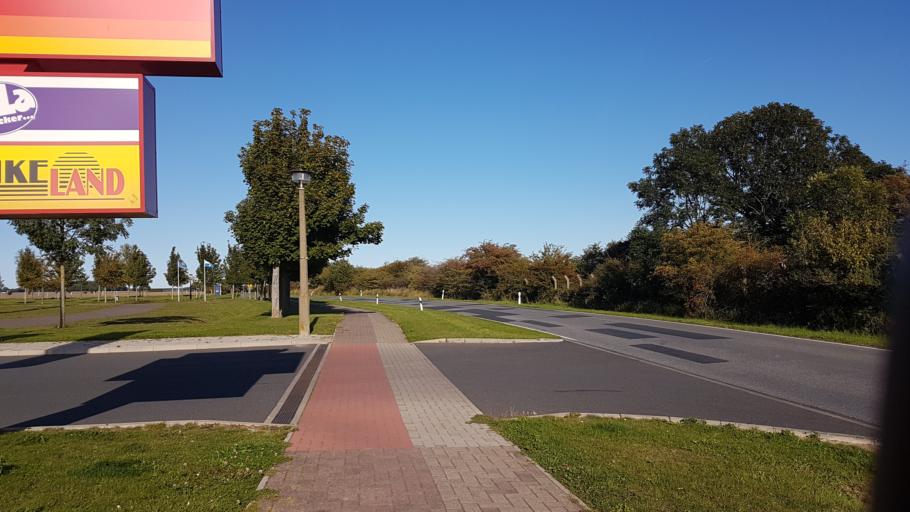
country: DE
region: Mecklenburg-Vorpommern
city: Dranske
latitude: 54.6315
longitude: 13.2377
